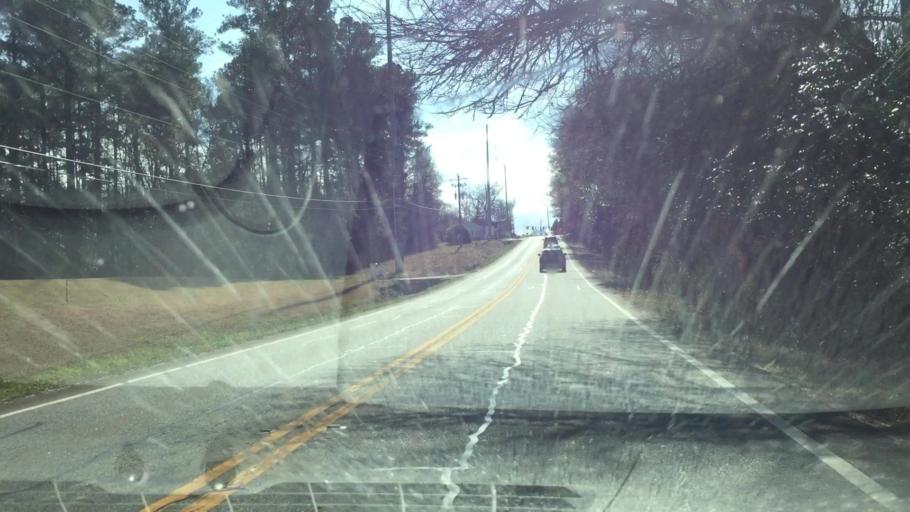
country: US
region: Georgia
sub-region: Henry County
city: McDonough
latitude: 33.4549
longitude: -84.1415
